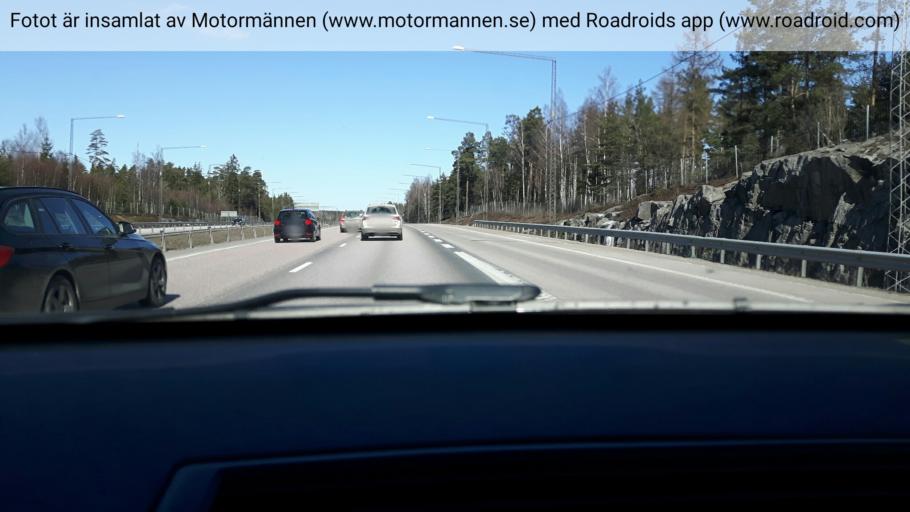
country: SE
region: Stockholm
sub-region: Sigtuna Kommun
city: Rosersberg
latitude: 59.6241
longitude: 17.9014
